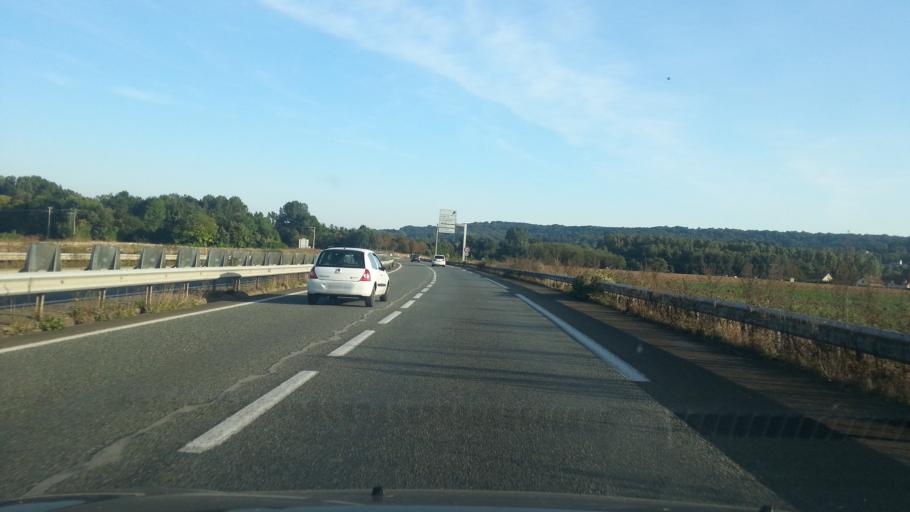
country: FR
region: Picardie
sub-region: Departement de l'Oise
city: Agnetz
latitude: 49.3934
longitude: 2.3802
